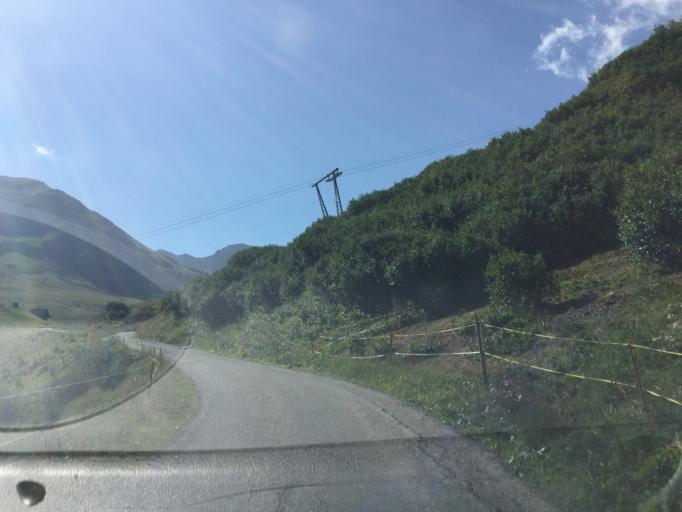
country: CH
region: Grisons
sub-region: Maloja District
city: Silvaplana
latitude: 46.4619
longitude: 9.6536
